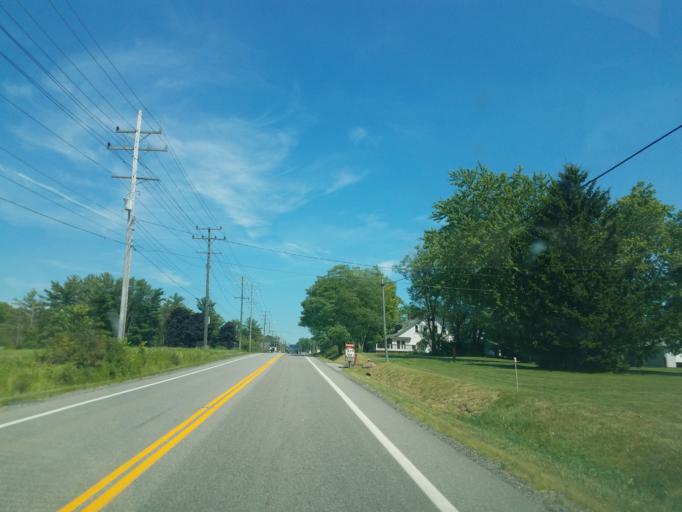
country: US
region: Ohio
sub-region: Geauga County
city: Chesterland
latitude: 41.5225
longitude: -81.3682
